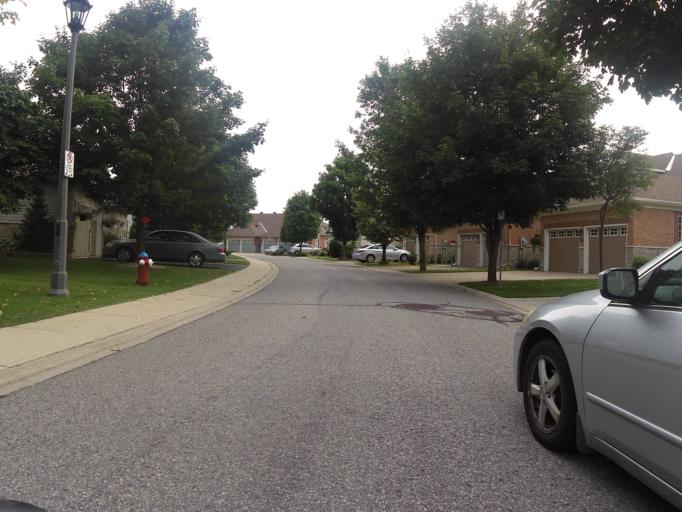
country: CA
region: Ontario
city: Bells Corners
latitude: 45.3152
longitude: -75.9254
